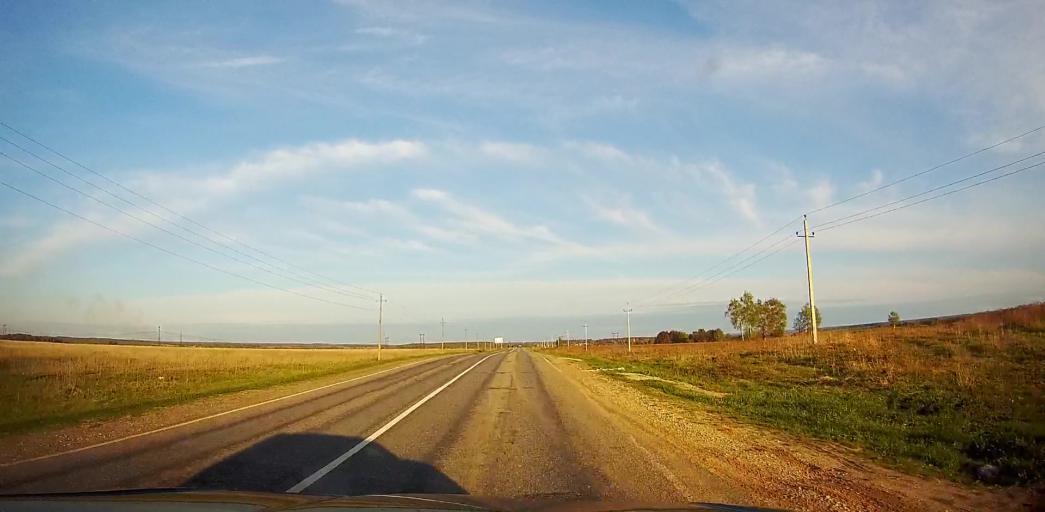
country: RU
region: Moskovskaya
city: Meshcherino
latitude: 55.2683
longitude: 38.2465
